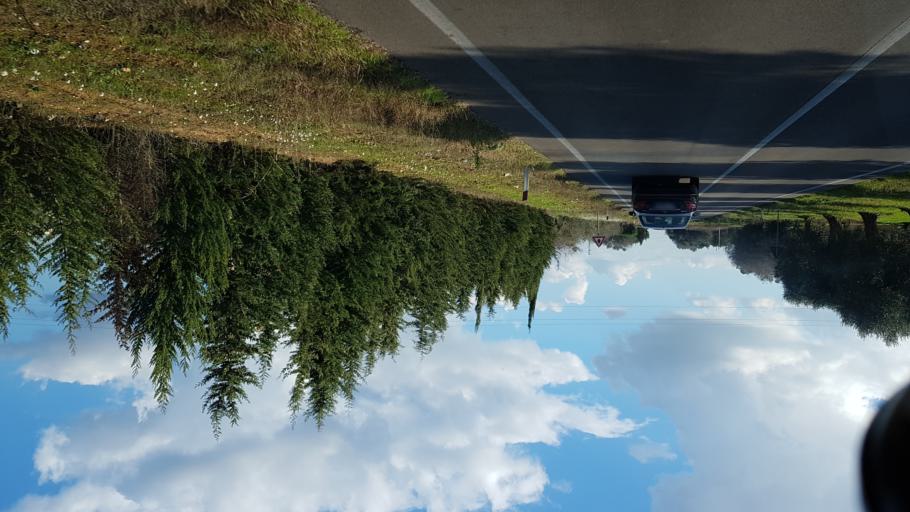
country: IT
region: Apulia
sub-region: Provincia di Lecce
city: Campi Salentina
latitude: 40.3992
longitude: 17.9998
